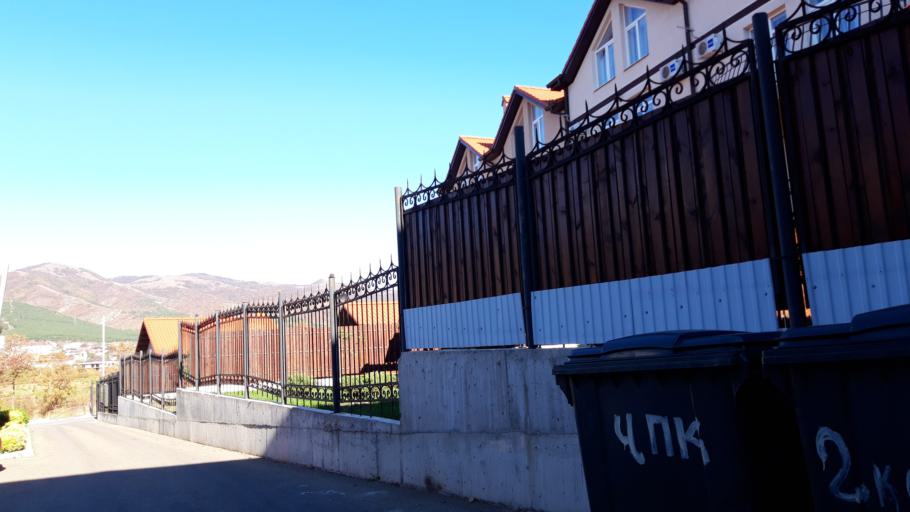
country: RU
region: Krasnodarskiy
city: Kabardinka
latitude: 44.6424
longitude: 37.9353
